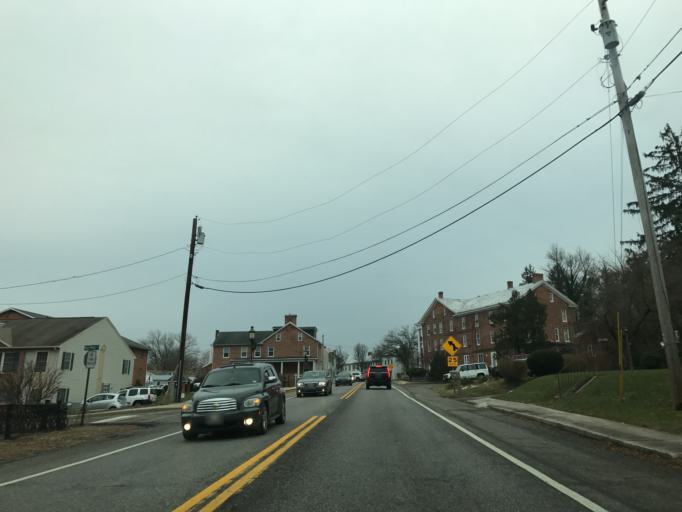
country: US
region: Maryland
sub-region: Frederick County
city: Emmitsburg
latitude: 39.7068
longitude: -77.3335
